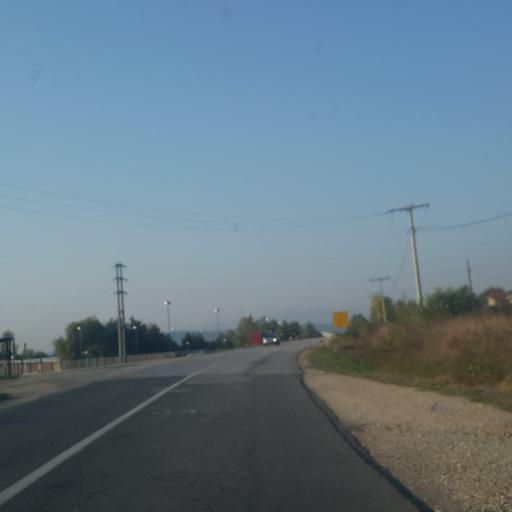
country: RS
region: Central Serbia
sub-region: Zajecarski Okrug
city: Zajecar
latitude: 43.9273
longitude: 22.2982
